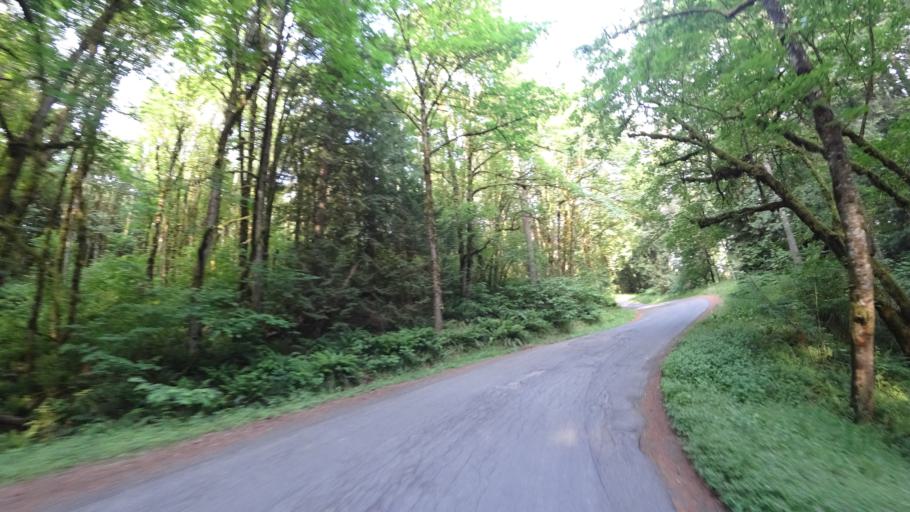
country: US
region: Oregon
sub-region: Clackamas County
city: Happy Valley
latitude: 45.4567
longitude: -122.4993
